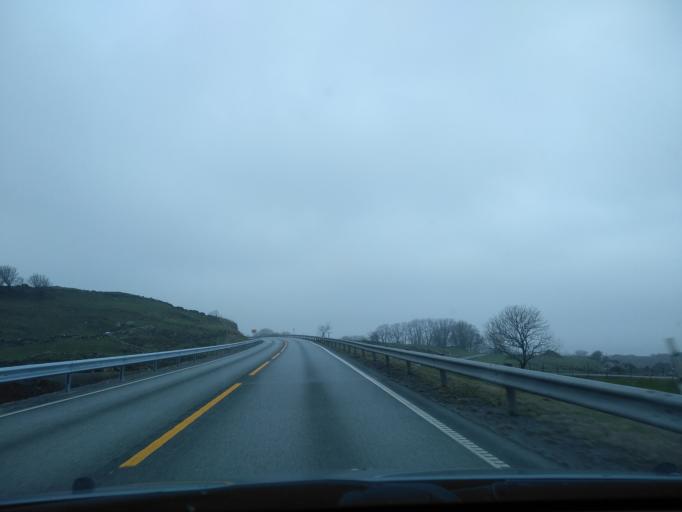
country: NO
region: Rogaland
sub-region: Rennesoy
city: Vikevag
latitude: 59.1261
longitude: 5.6489
